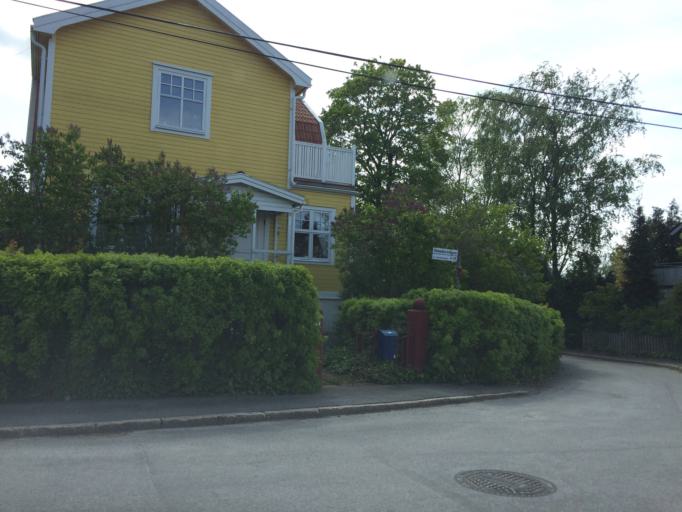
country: SE
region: Stockholm
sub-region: Huddinge Kommun
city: Huddinge
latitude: 59.2764
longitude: 18.0024
